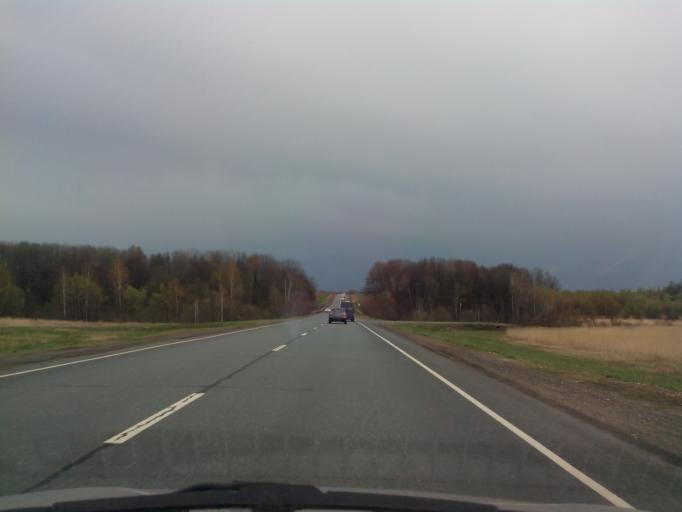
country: RU
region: Moskovskaya
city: Uzunovo
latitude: 54.5478
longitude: 38.4661
